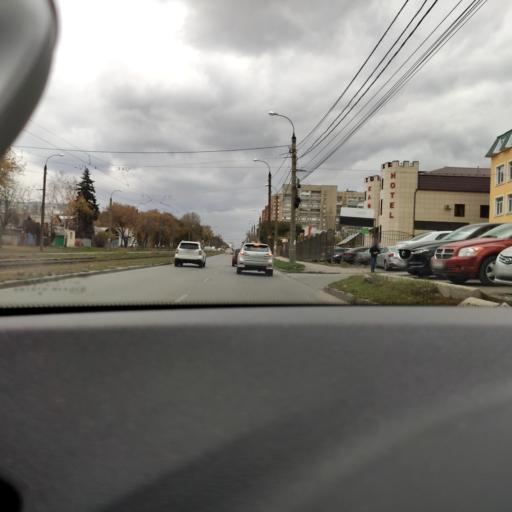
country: RU
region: Samara
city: Samara
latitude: 53.2296
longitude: 50.2279
